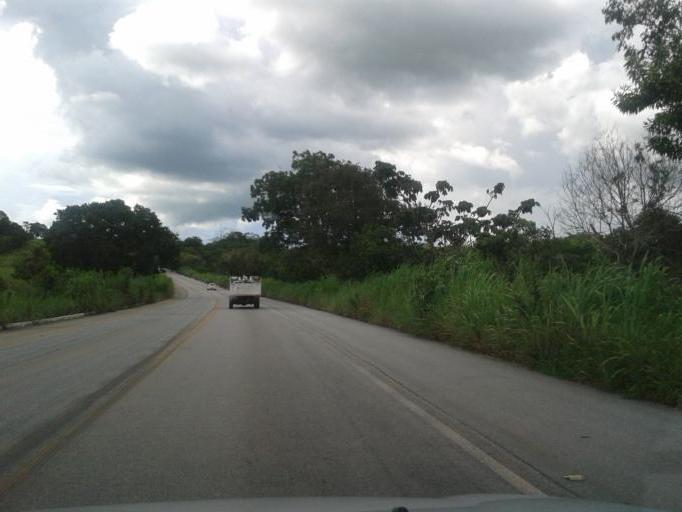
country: BR
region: Goias
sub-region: Goias
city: Goias
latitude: -15.8641
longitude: -50.0888
